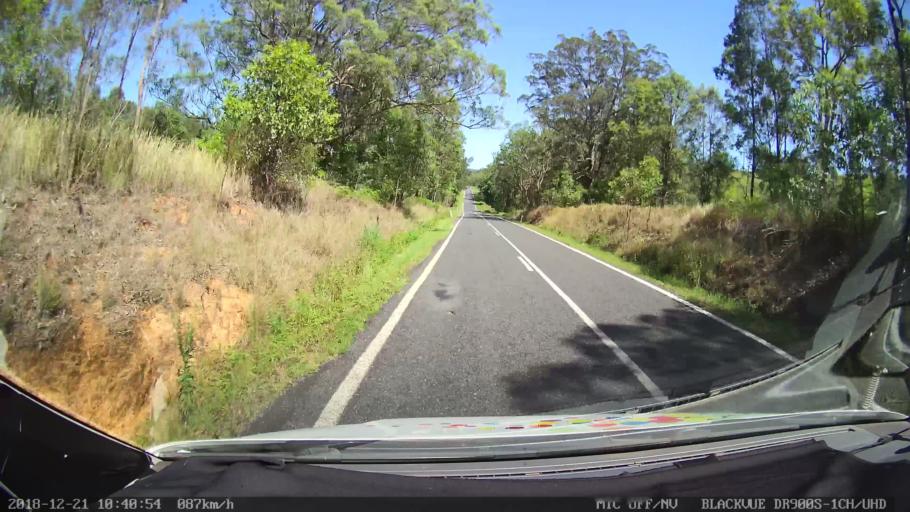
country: AU
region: New South Wales
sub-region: Clarence Valley
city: Gordon
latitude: -29.5952
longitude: 152.5814
